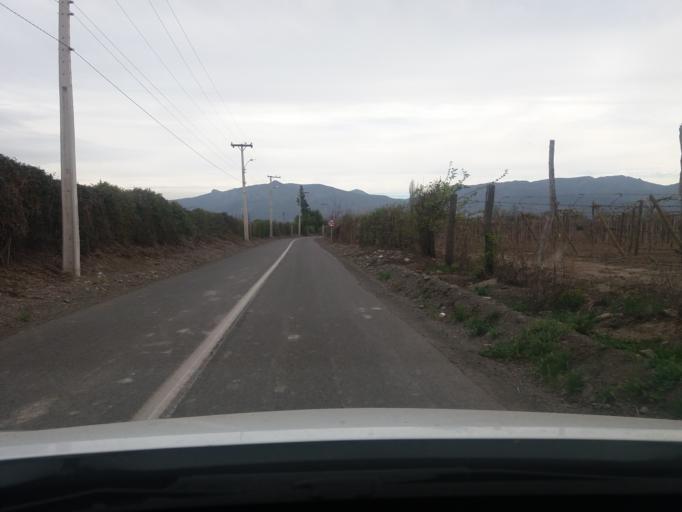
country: CL
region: Valparaiso
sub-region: Provincia de Los Andes
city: Los Andes
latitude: -32.8515
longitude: -70.6383
